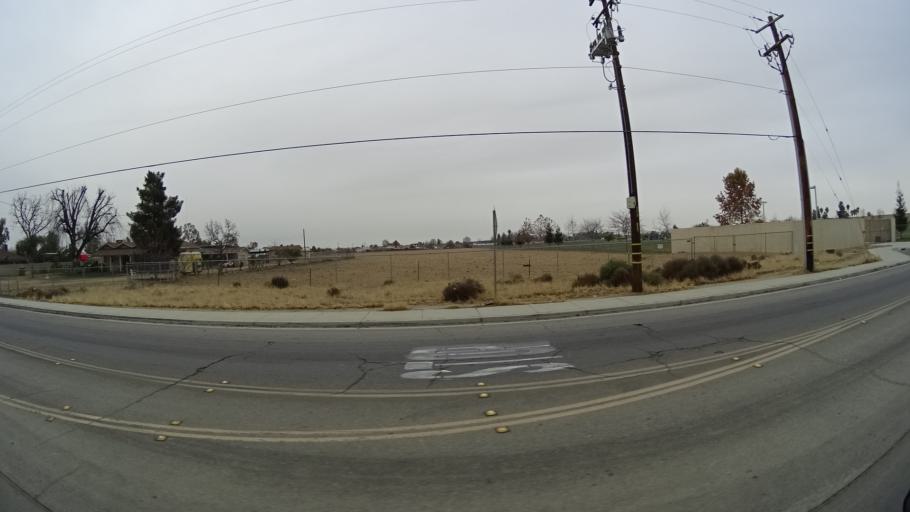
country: US
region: California
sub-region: Kern County
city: Lamont
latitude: 35.3446
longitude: -118.9319
